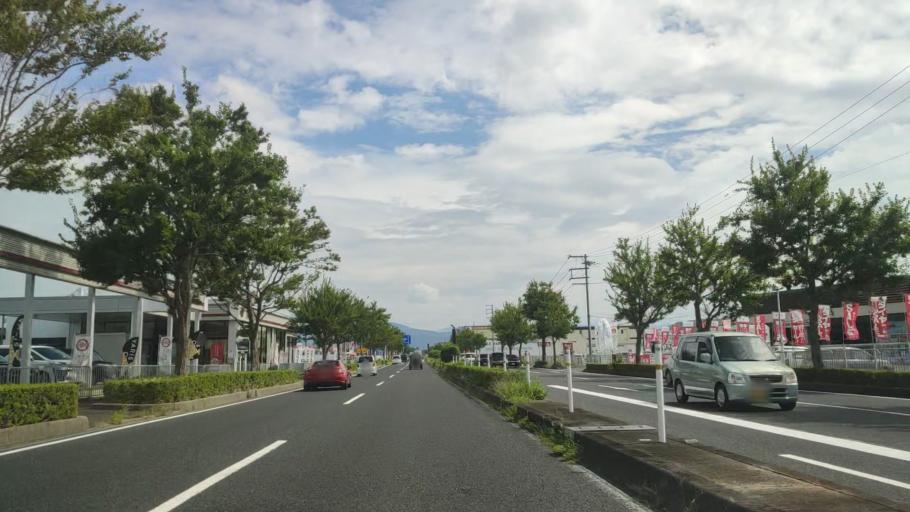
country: JP
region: Wakayama
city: Iwade
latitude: 34.2630
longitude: 135.2898
